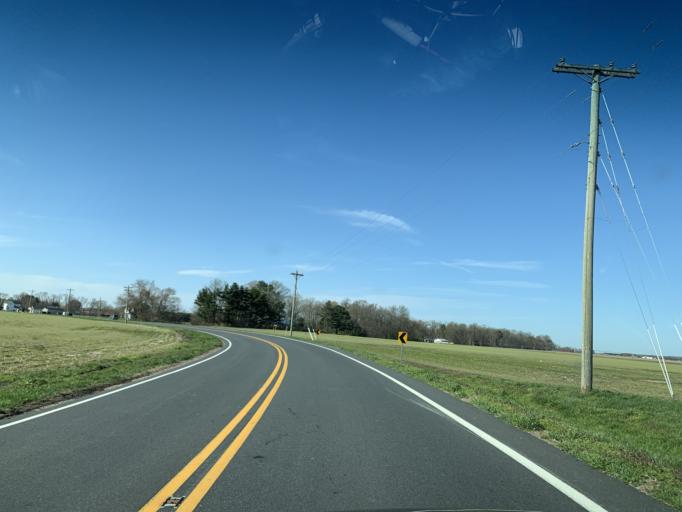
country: US
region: Delaware
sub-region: Sussex County
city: Milford
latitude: 38.9535
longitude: -75.4744
